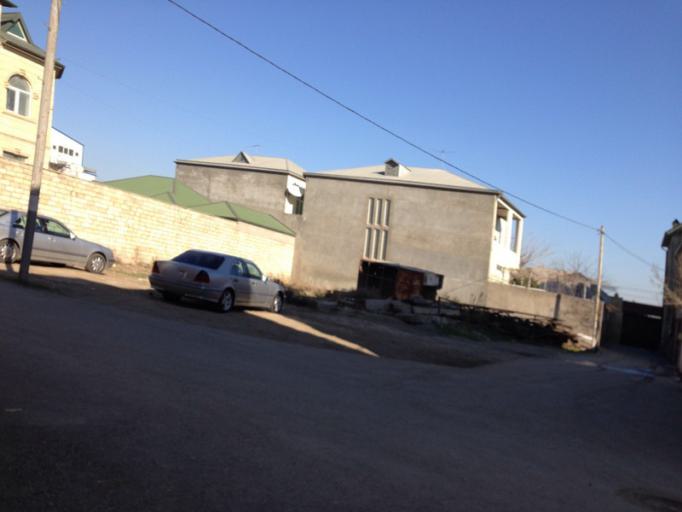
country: AZ
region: Baki
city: Baku
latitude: 40.4215
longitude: 49.8653
